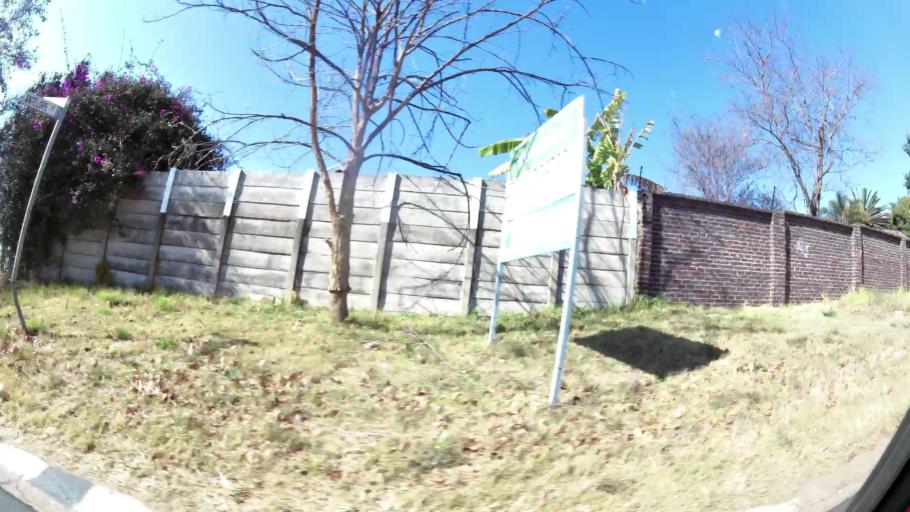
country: ZA
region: Gauteng
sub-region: City of Johannesburg Metropolitan Municipality
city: Roodepoort
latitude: -26.1371
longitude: 27.9109
